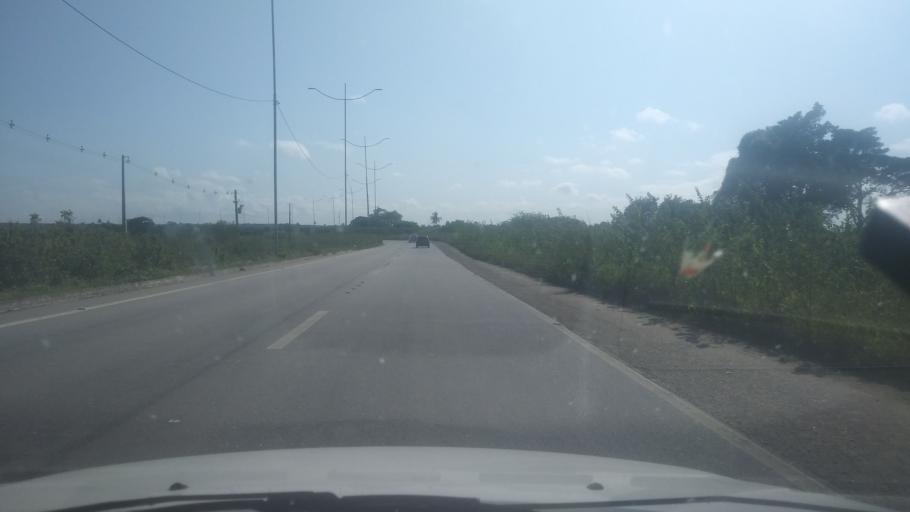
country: BR
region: Rio Grande do Norte
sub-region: Sao Goncalo Do Amarante
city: Sao Goncalo do Amarante
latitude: -5.8161
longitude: -35.3628
